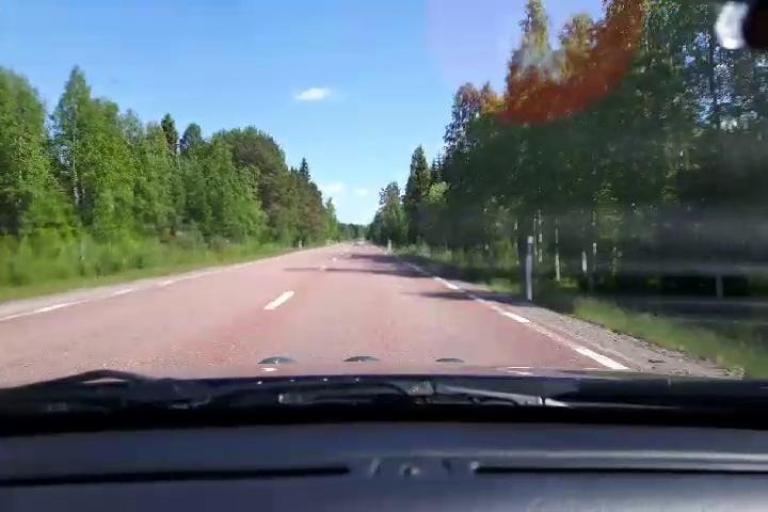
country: SE
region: Gaevleborg
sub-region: Hudiksvalls Kommun
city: Delsbo
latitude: 61.7697
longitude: 16.6927
